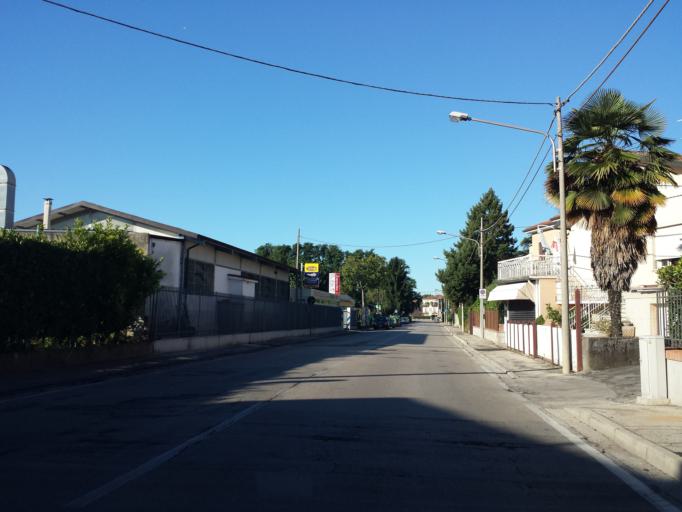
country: IT
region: Veneto
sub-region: Provincia di Vicenza
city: Vicenza
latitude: 45.5606
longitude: 11.5558
